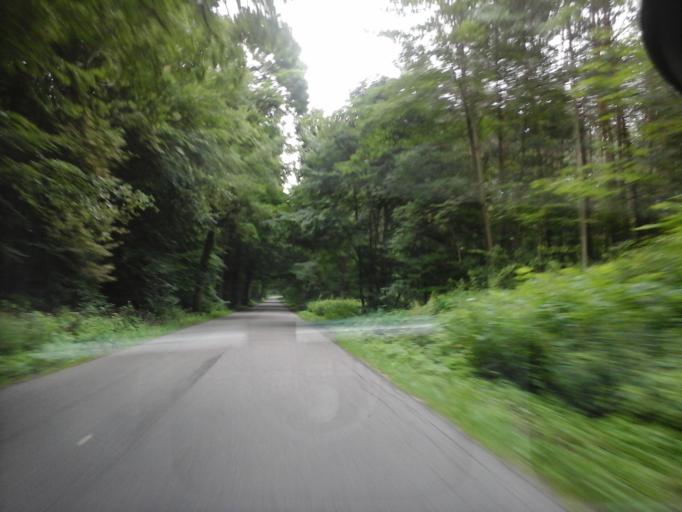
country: PL
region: West Pomeranian Voivodeship
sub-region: Powiat choszczenski
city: Bierzwnik
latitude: 53.0147
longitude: 15.6406
